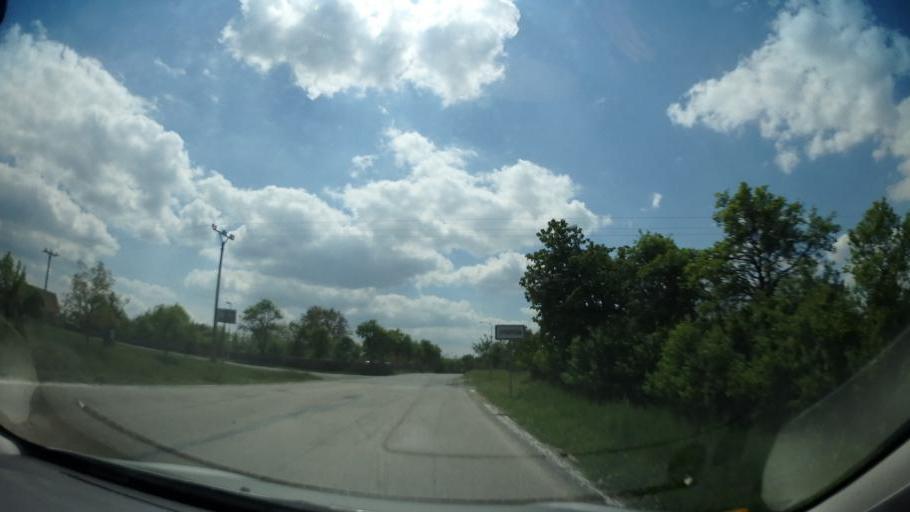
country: CZ
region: Vysocina
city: Hrotovice
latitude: 49.1559
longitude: 16.0772
